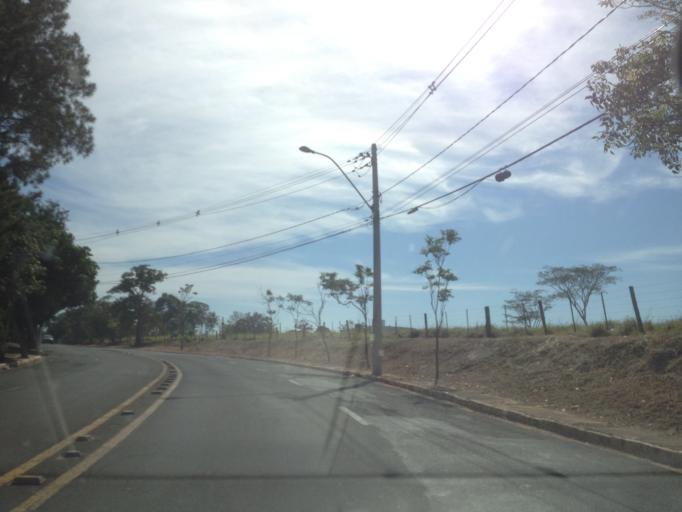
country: BR
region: Sao Paulo
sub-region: Marilia
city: Marilia
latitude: -22.2008
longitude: -49.9309
